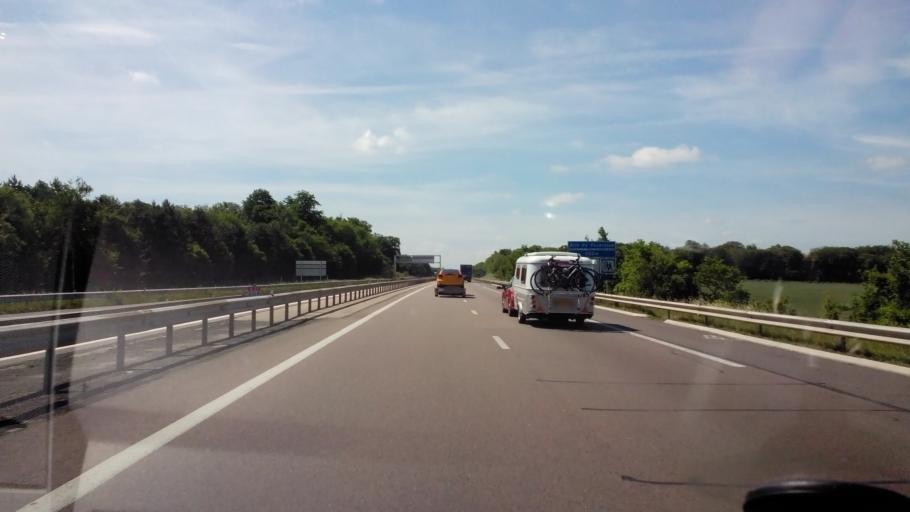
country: FR
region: Lorraine
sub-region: Departement de Meurthe-et-Moselle
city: Colombey-les-Belles
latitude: 48.5166
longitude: 5.9146
